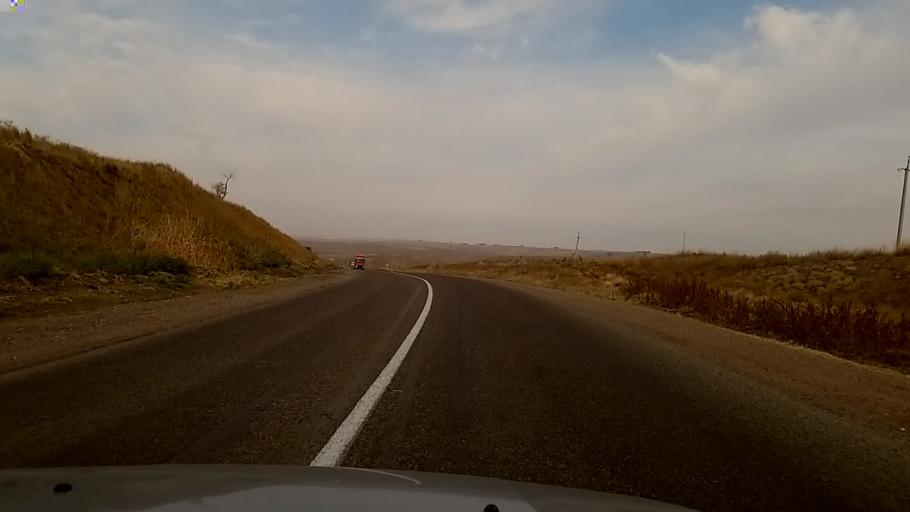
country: KZ
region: Almaty Oblysy
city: Burunday
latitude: 43.4953
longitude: 76.6620
